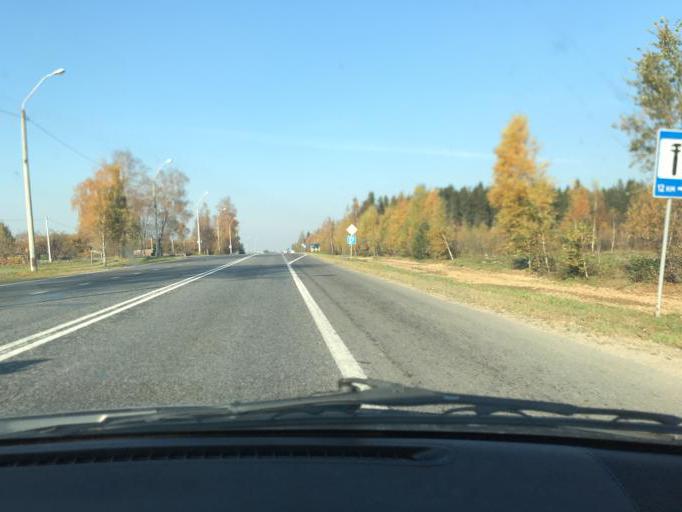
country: BY
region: Vitebsk
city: Orsha
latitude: 54.3912
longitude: 30.4434
